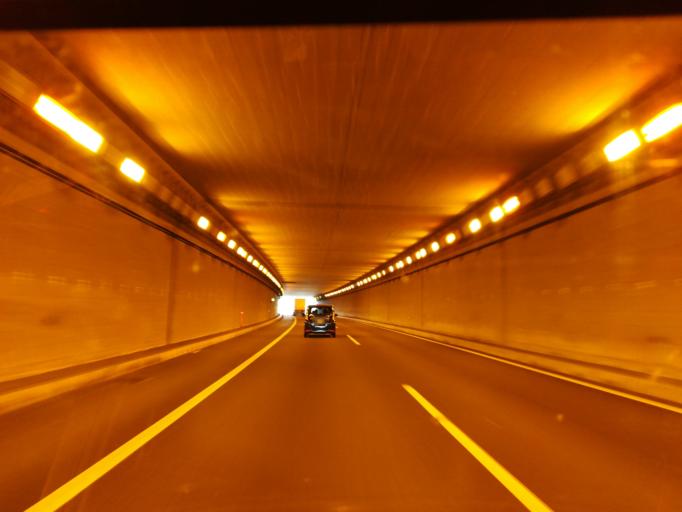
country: JP
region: Saitama
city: Sayama
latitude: 35.8326
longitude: 139.3739
